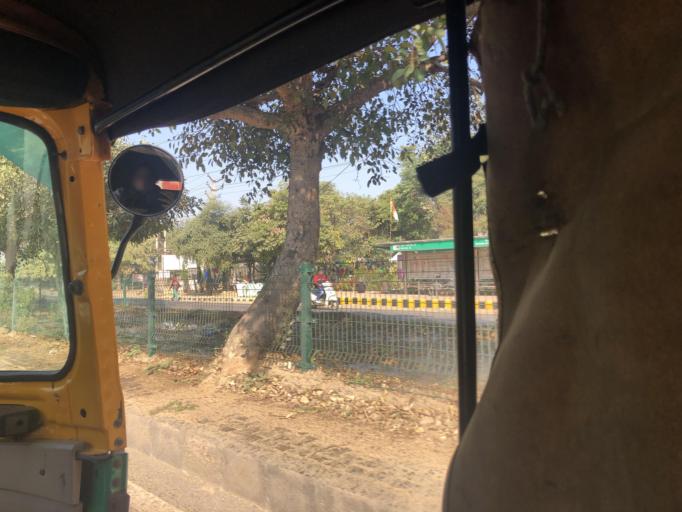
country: IN
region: Haryana
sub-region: Gurgaon
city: Gurgaon
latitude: 28.4421
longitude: 77.0852
